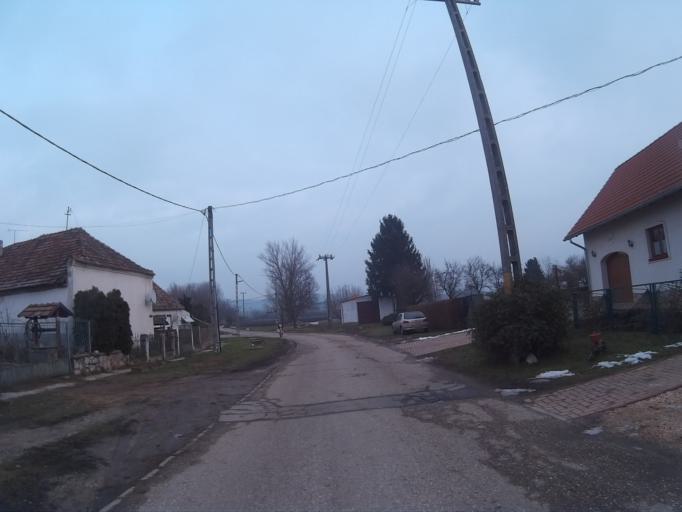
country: HU
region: Komarom-Esztergom
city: Tarjan
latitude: 47.6438
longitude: 18.5161
